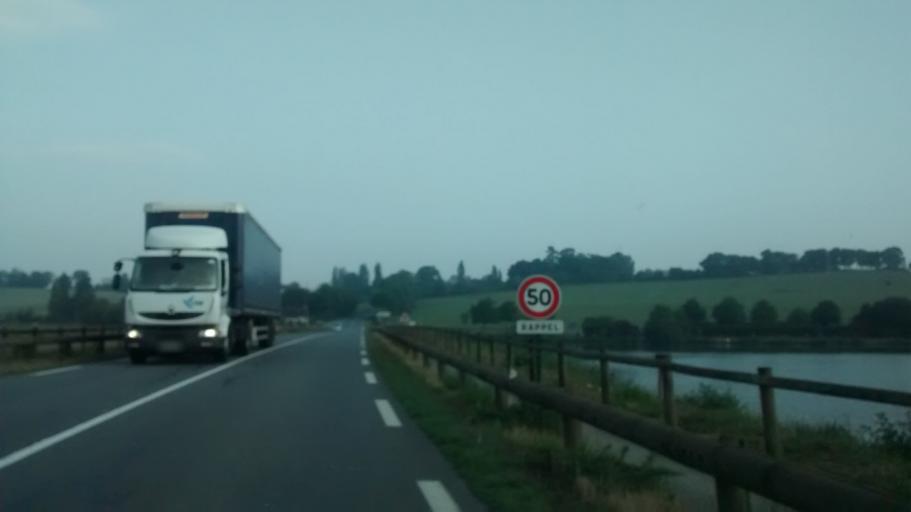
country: FR
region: Brittany
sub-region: Departement d'Ille-et-Vilaine
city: Montreuil-sous-Perouse
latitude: 48.1437
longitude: -1.2528
